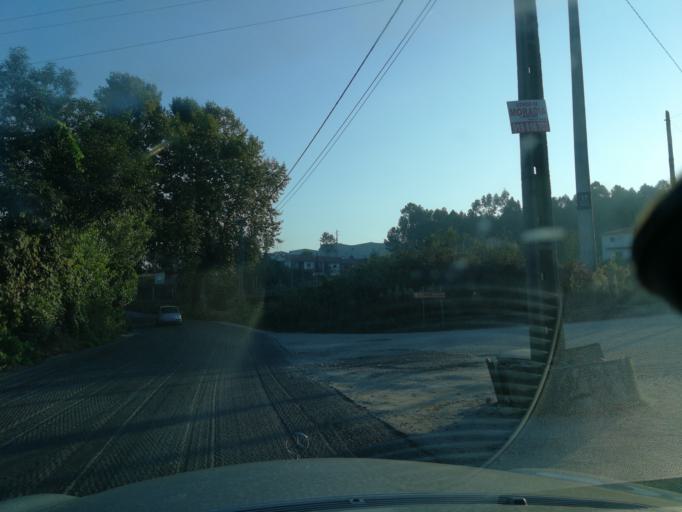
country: PT
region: Braga
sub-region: Braga
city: Braga
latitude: 41.5213
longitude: -8.4330
